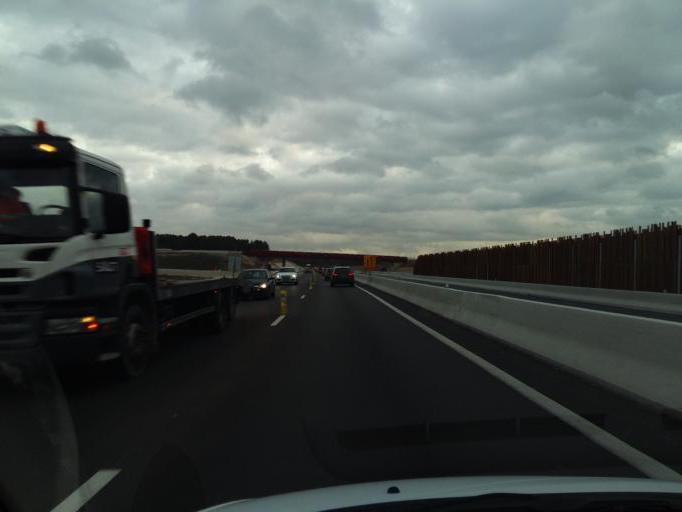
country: FR
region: Provence-Alpes-Cote d'Azur
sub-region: Departement des Bouches-du-Rhone
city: Cabries
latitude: 43.4619
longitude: 5.3360
